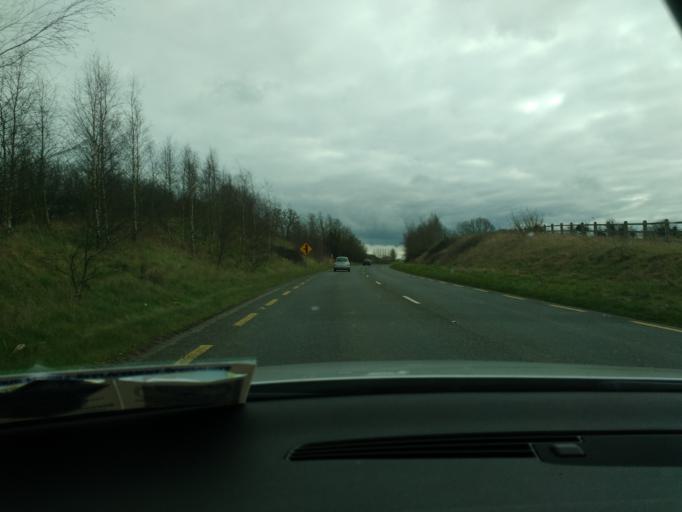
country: IE
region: Leinster
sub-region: Kilkenny
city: Ballyragget
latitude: 52.7167
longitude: -7.3343
